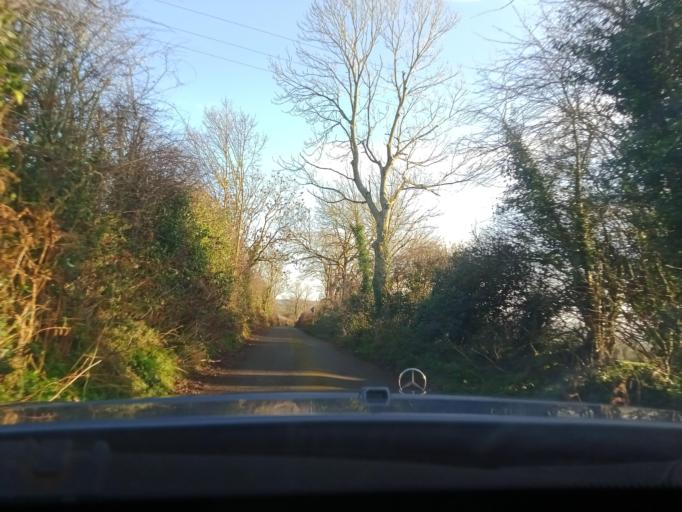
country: IE
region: Munster
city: Carrick-on-Suir
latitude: 52.4363
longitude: -7.4157
